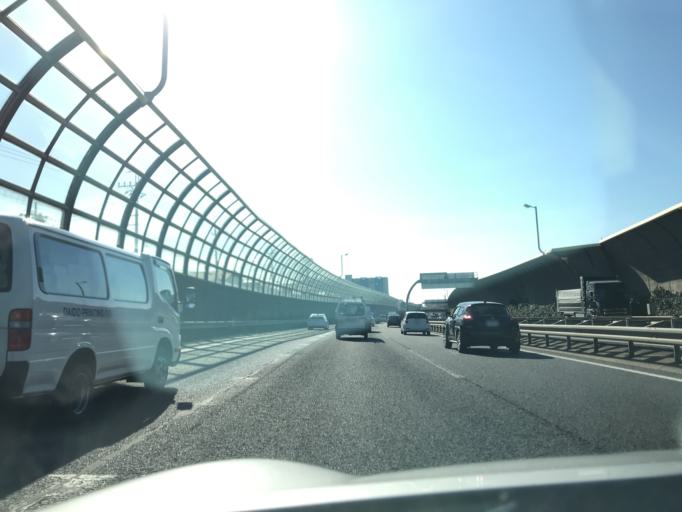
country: JP
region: Chiba
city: Chiba
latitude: 35.6567
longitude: 140.1054
